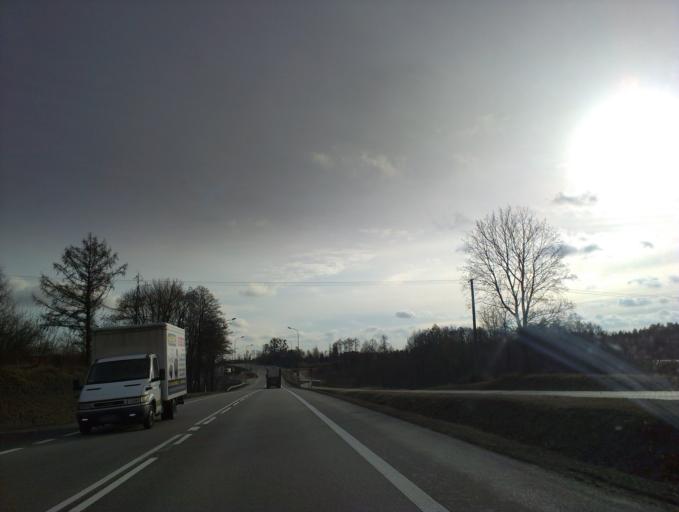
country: PL
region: Kujawsko-Pomorskie
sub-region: Powiat lipnowski
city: Lipno
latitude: 52.8636
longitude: 19.1551
